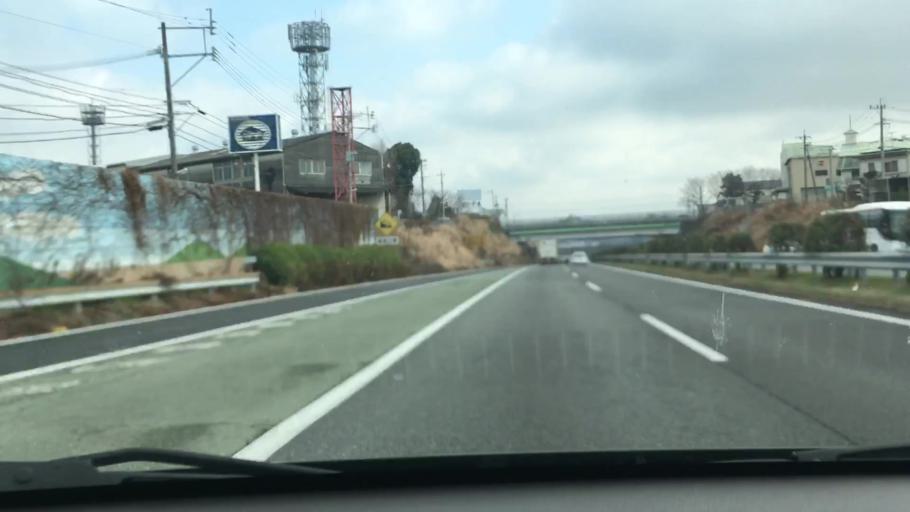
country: JP
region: Kumamoto
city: Kumamoto
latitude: 32.8496
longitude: 130.7664
